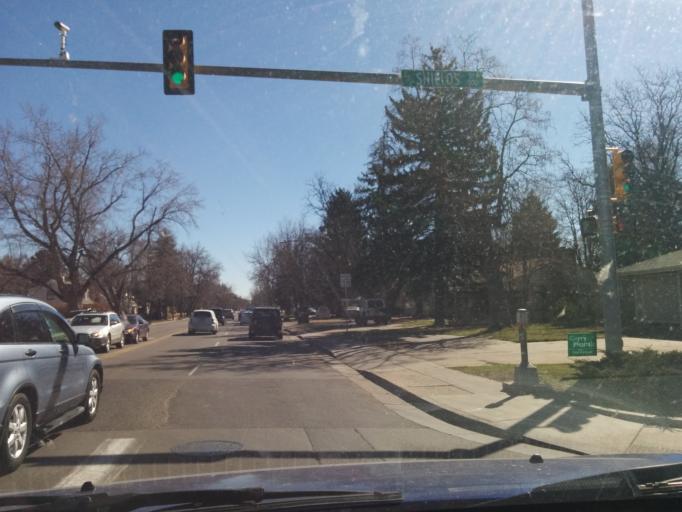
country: US
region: Colorado
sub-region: Larimer County
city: Fort Collins
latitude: 40.5817
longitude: -105.0959
